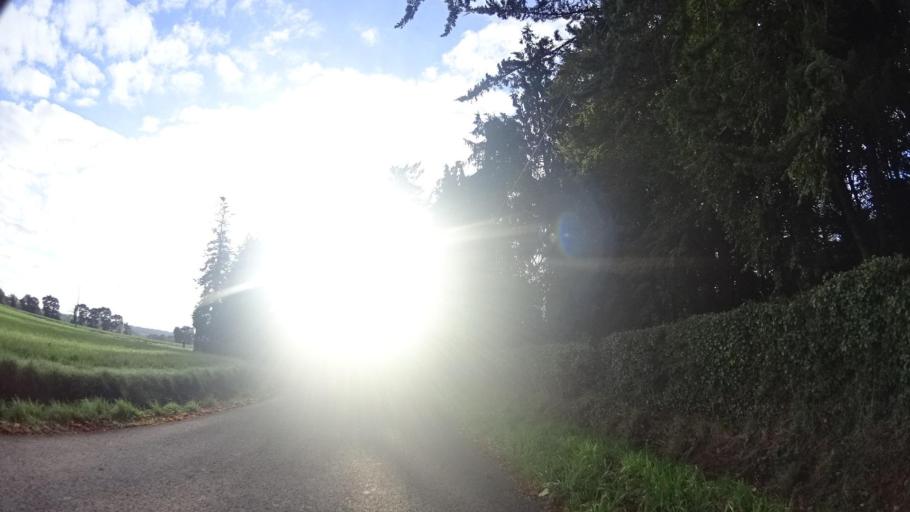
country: FR
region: Brittany
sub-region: Departement des Cotes-d'Armor
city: Evran
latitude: 48.3570
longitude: -1.9473
